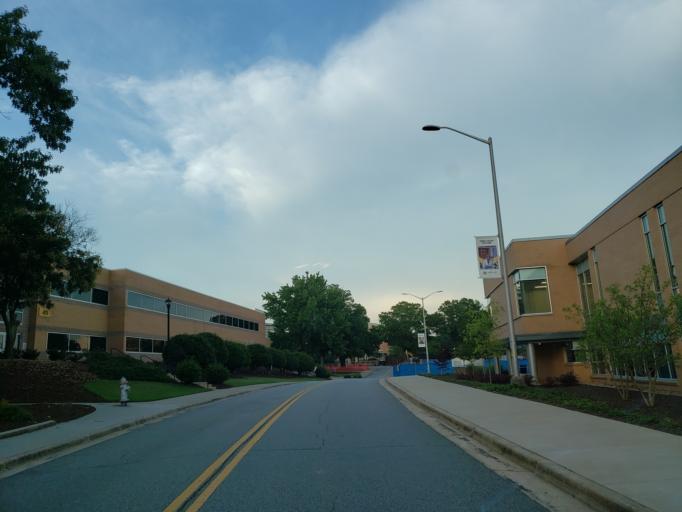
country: US
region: Georgia
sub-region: Cobb County
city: Kennesaw
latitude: 34.0399
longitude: -84.5843
